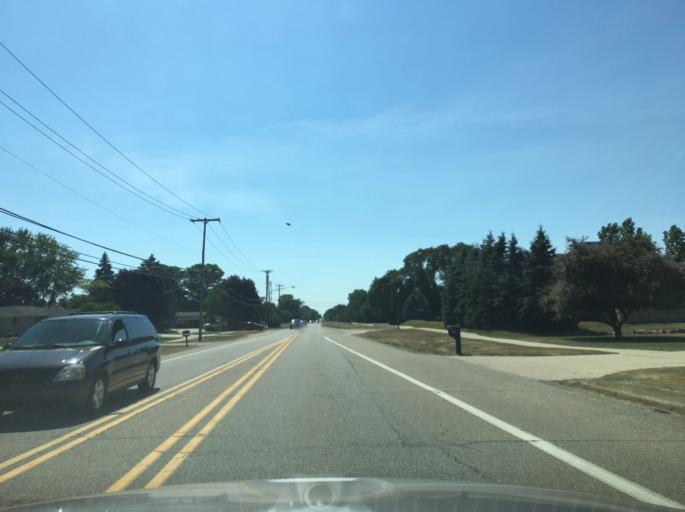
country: US
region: Michigan
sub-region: Macomb County
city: Utica
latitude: 42.6412
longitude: -82.9962
